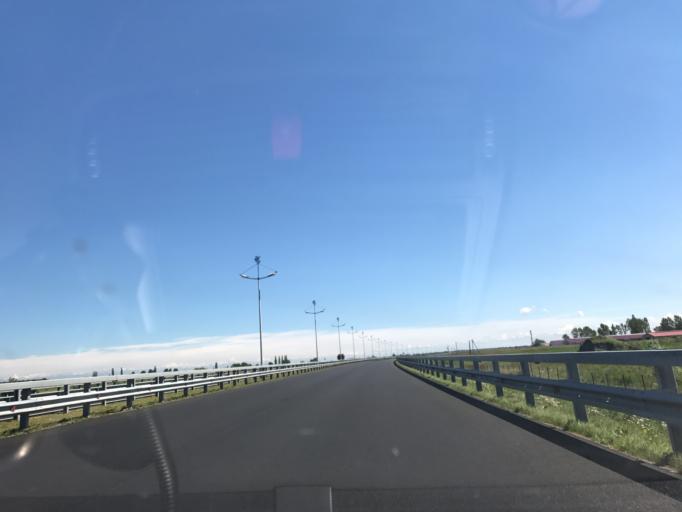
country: RU
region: Kaliningrad
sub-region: Zelenogradskiy Rayon
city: Zelenogradsk
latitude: 54.9203
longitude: 20.4601
